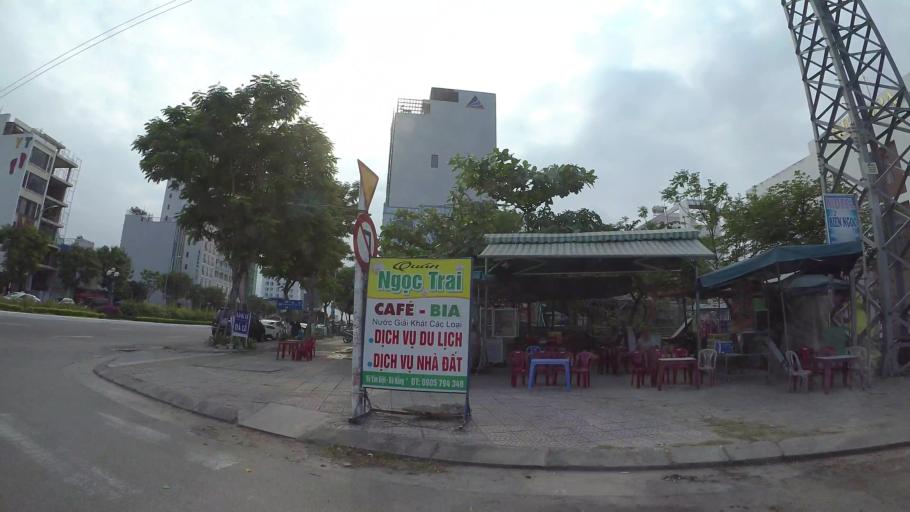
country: VN
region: Da Nang
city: Son Tra
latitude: 16.0624
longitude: 108.2385
